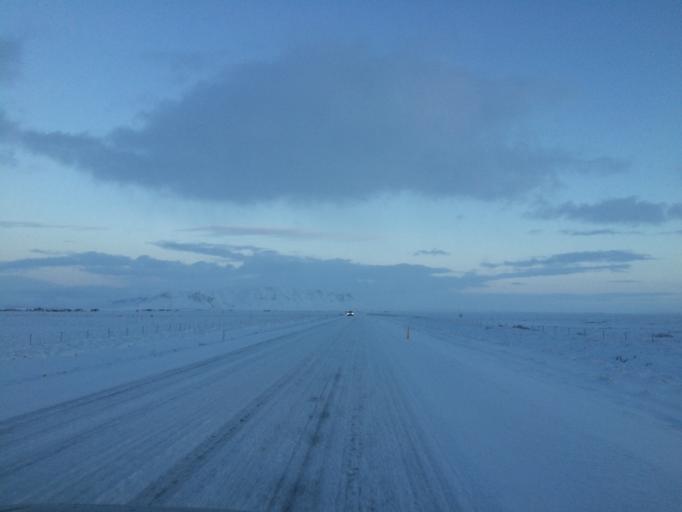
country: IS
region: South
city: Selfoss
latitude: 63.8812
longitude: -21.0874
